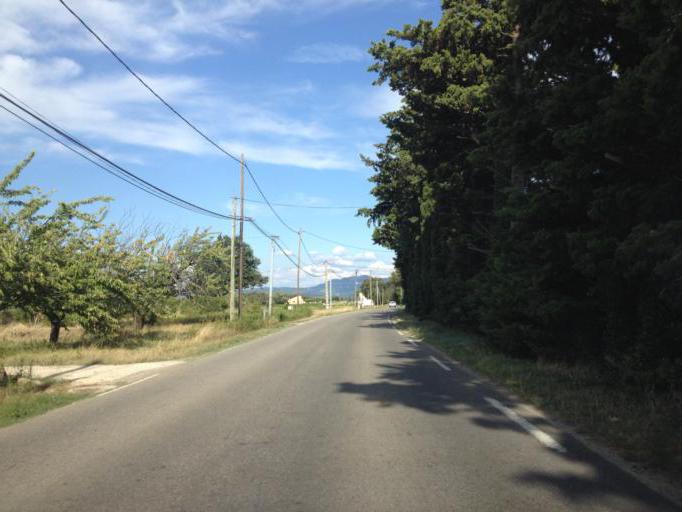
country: FR
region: Provence-Alpes-Cote d'Azur
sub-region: Departement du Vaucluse
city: Camaret-sur-Aigues
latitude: 44.1634
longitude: 4.8906
